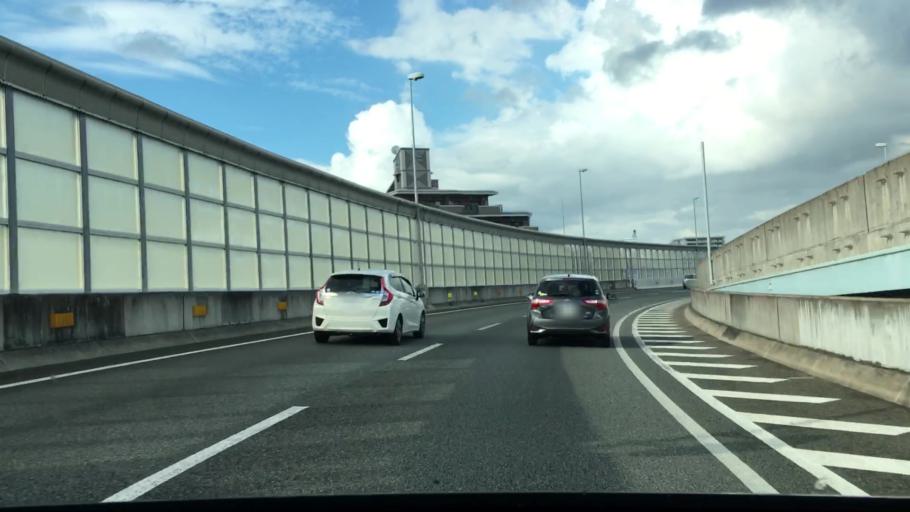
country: JP
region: Fukuoka
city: Fukuoka-shi
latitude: 33.5770
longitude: 130.3159
